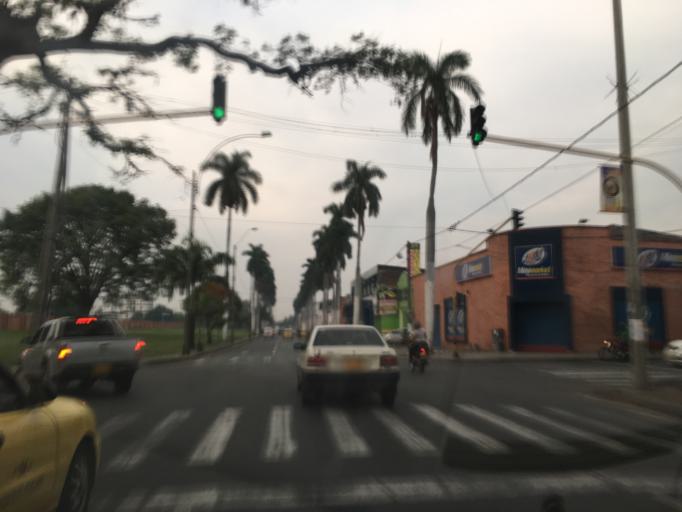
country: CO
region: Valle del Cauca
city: Cali
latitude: 3.4572
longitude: -76.5203
